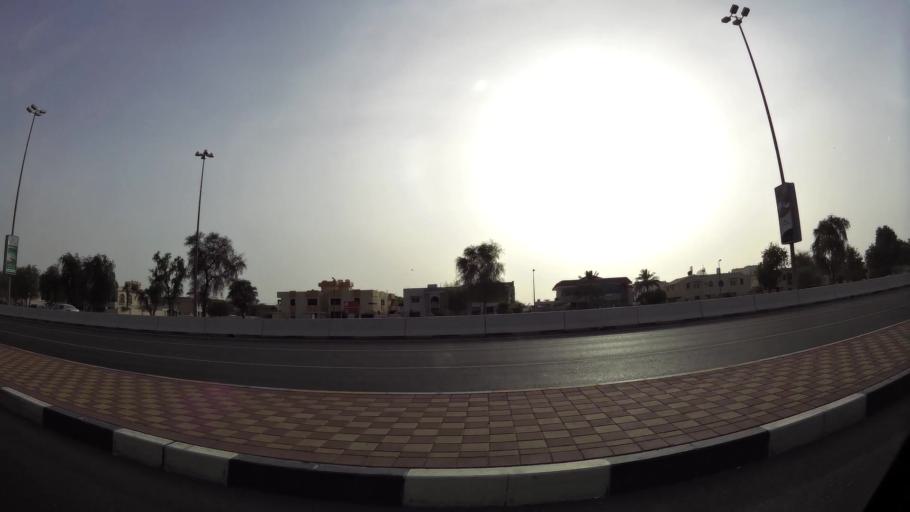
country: AE
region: Abu Dhabi
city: Al Ain
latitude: 24.2390
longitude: 55.7196
